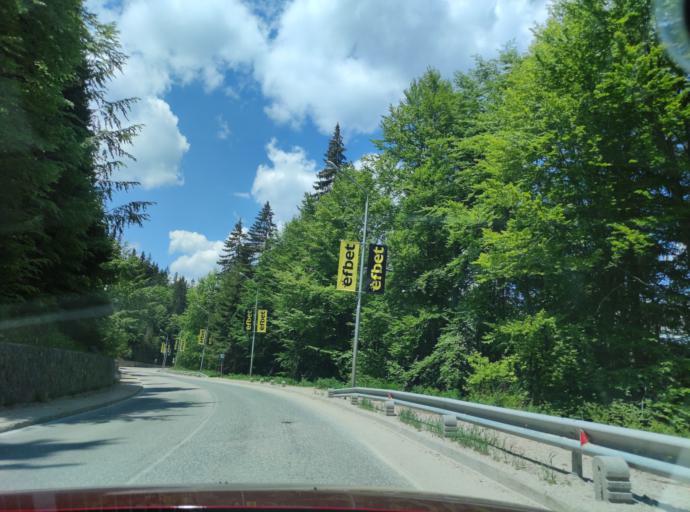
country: BG
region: Smolyan
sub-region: Obshtina Smolyan
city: Smolyan
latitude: 41.6390
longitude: 24.6954
